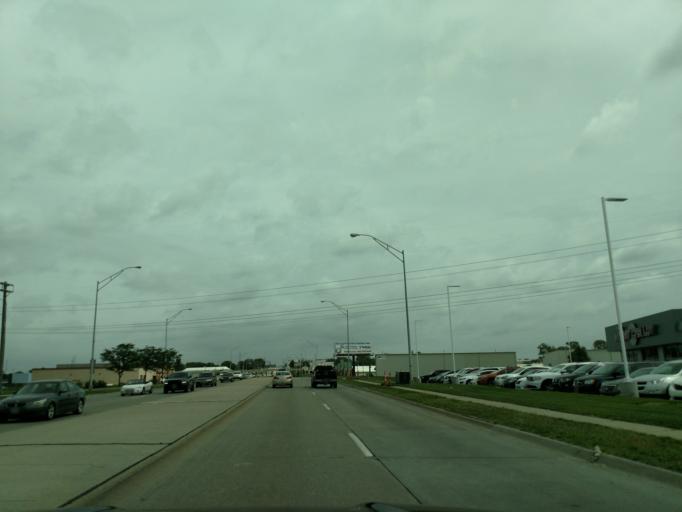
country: US
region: Nebraska
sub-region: Douglas County
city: Ralston
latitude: 41.2074
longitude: -96.0238
